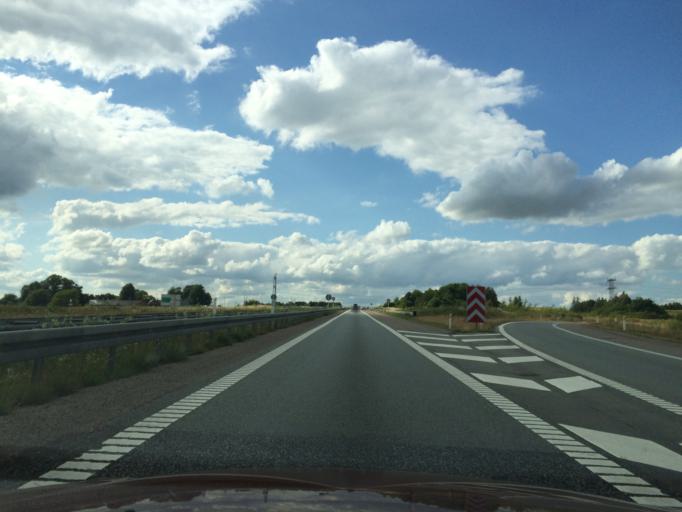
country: DK
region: Central Jutland
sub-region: Arhus Kommune
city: Trige
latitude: 56.2243
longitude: 10.1227
